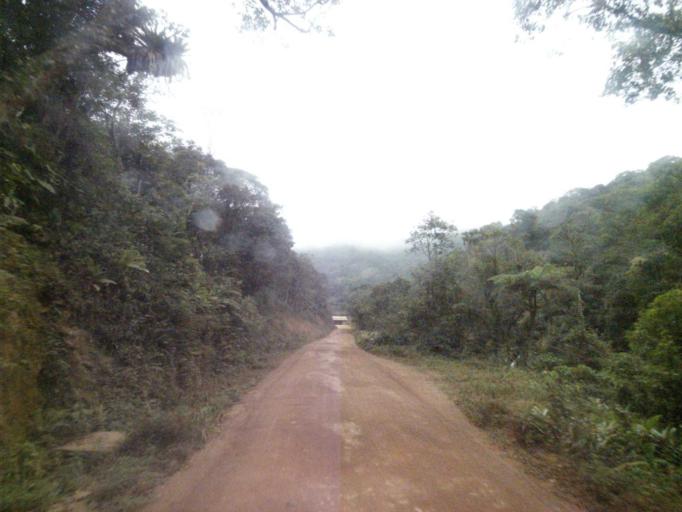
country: BR
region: Santa Catarina
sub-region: Anitapolis
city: Anitapolis
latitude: -27.8964
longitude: -49.1299
